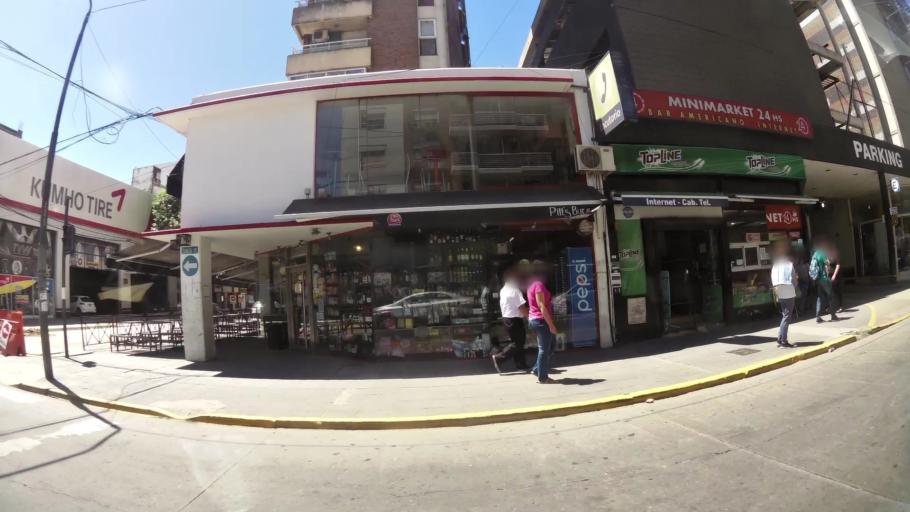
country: AR
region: Santa Fe
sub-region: Departamento de Rosario
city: Rosario
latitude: -32.9400
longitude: -60.6663
